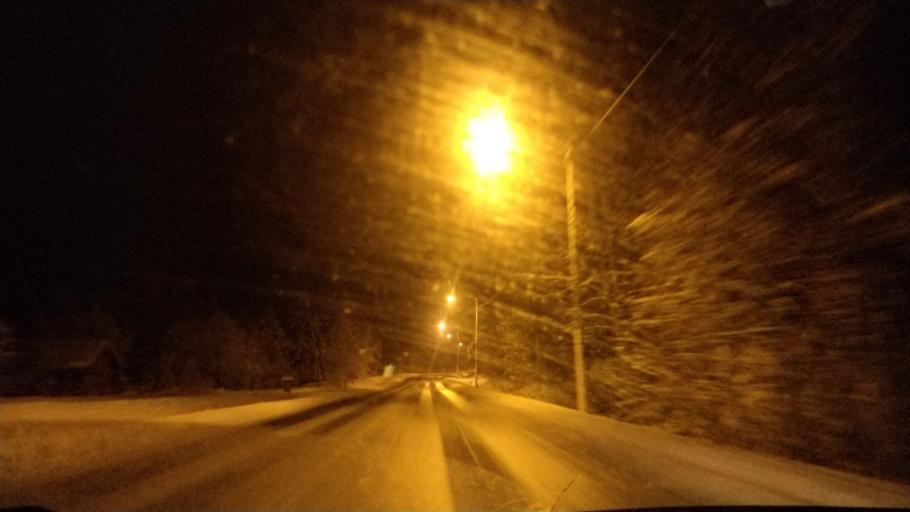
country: FI
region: Lapland
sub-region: Rovaniemi
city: Rovaniemi
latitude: 66.4005
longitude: 25.3883
